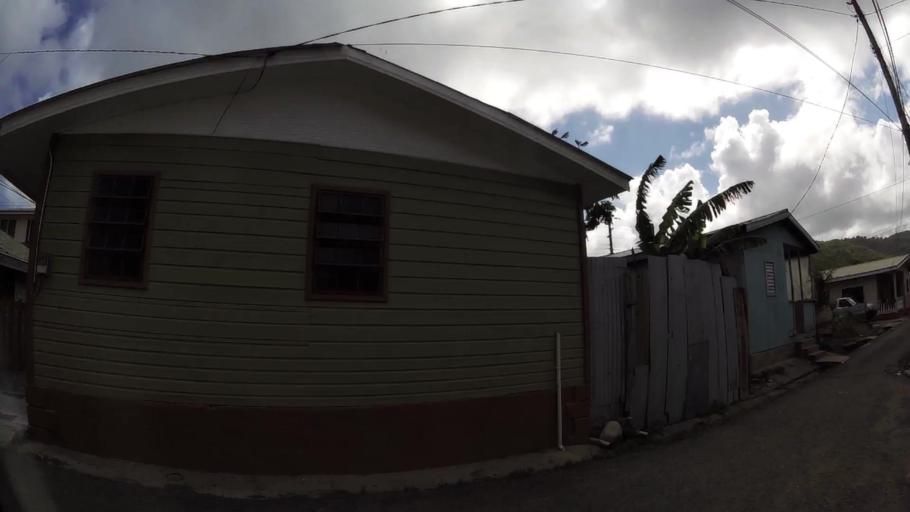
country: LC
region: Dennery Quarter
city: Dennery
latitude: 13.9112
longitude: -60.8889
